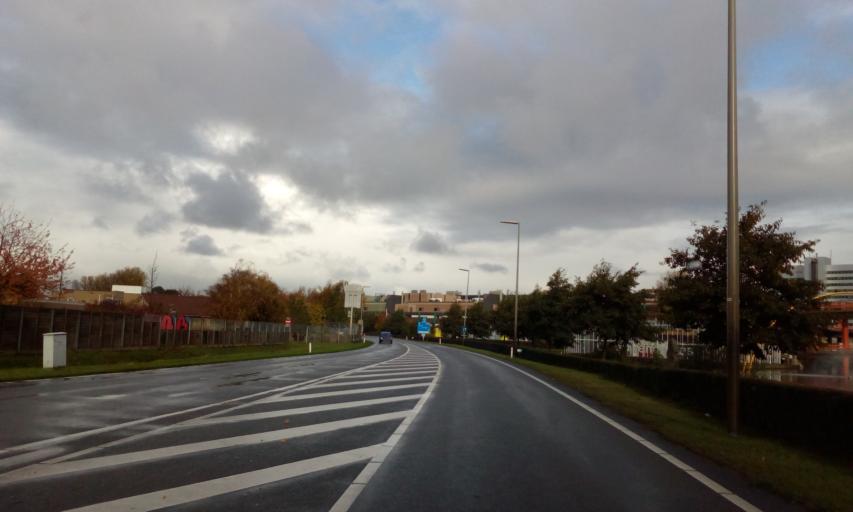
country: NL
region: South Holland
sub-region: Gemeente Westland
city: Honselersdijk
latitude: 51.9940
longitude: 4.2236
